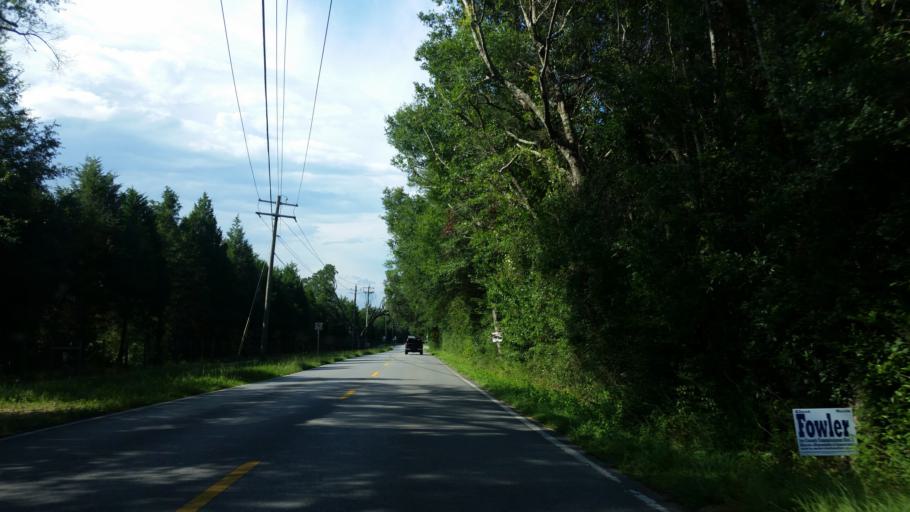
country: US
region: Florida
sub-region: Santa Rosa County
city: Pace
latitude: 30.6288
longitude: -87.1313
